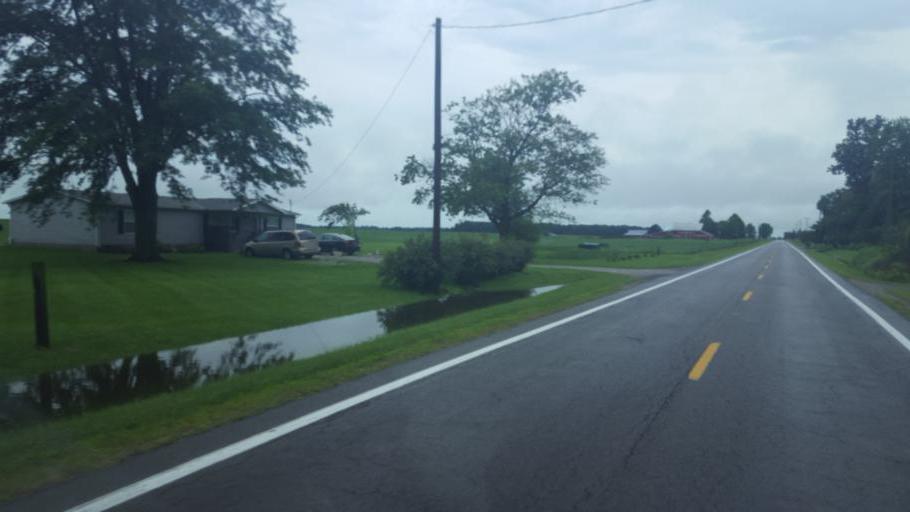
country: US
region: Ohio
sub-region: Union County
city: Richwood
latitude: 40.5081
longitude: -83.2676
